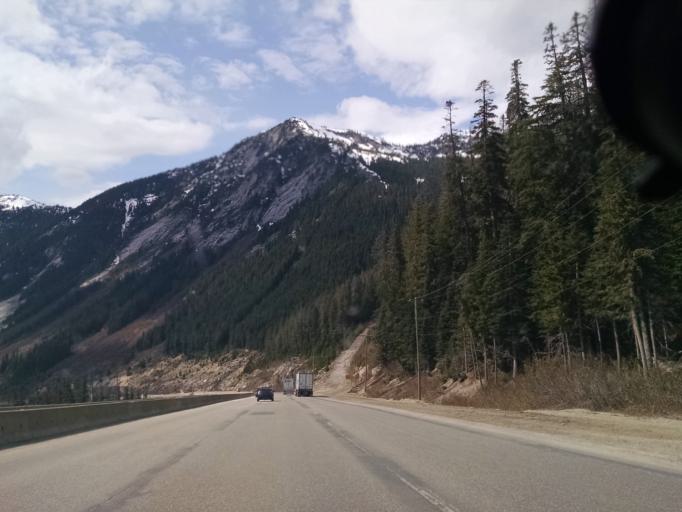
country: CA
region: British Columbia
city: Hope
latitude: 49.5980
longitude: -121.1480
